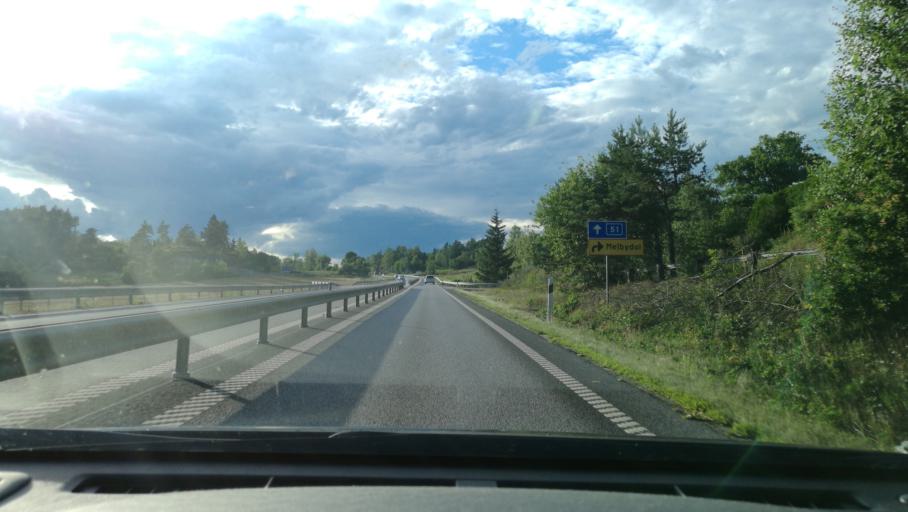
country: SE
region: OEstergoetland
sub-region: Norrkopings Kommun
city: Svartinge
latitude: 58.6827
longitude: 15.9390
